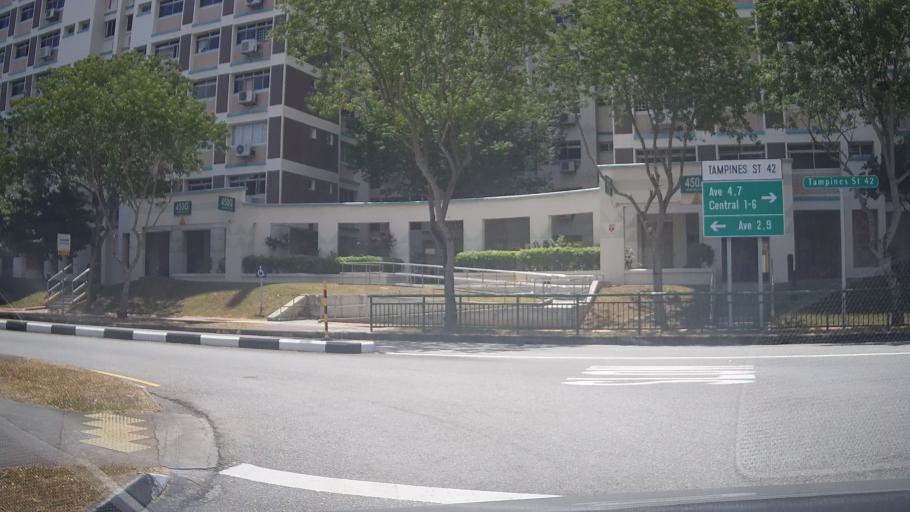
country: SG
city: Singapore
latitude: 1.3587
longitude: 103.9524
